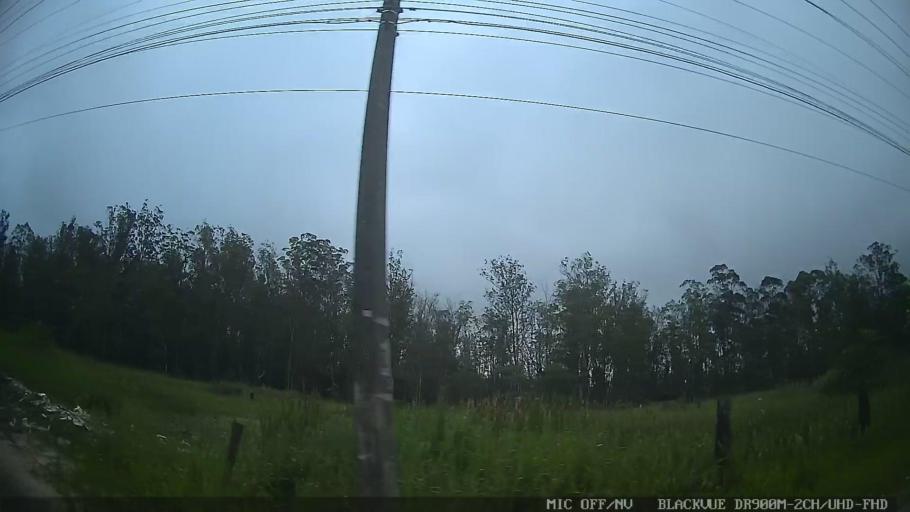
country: BR
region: Sao Paulo
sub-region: Mogi das Cruzes
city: Mogi das Cruzes
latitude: -23.5203
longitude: -46.1533
